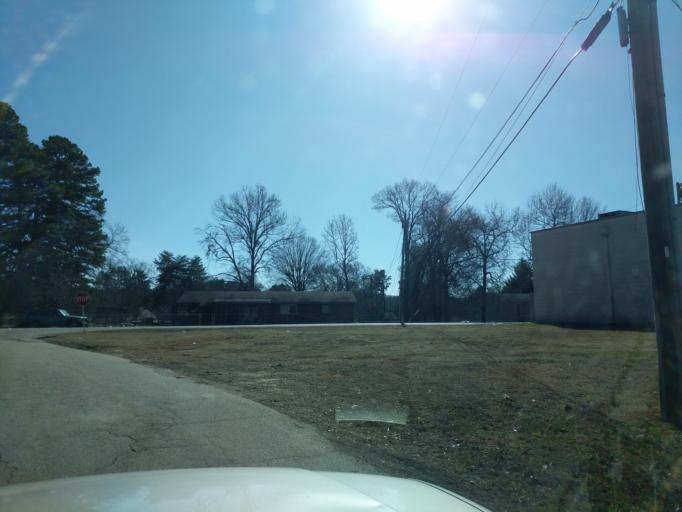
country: US
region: South Carolina
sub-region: Anderson County
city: Homeland Park
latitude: 34.4478
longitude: -82.7022
